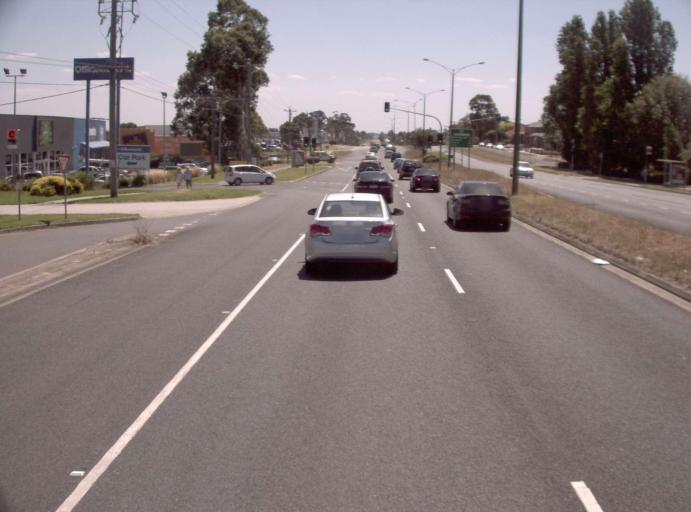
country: AU
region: Victoria
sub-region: Knox
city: Boronia
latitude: -37.8819
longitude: 145.2747
